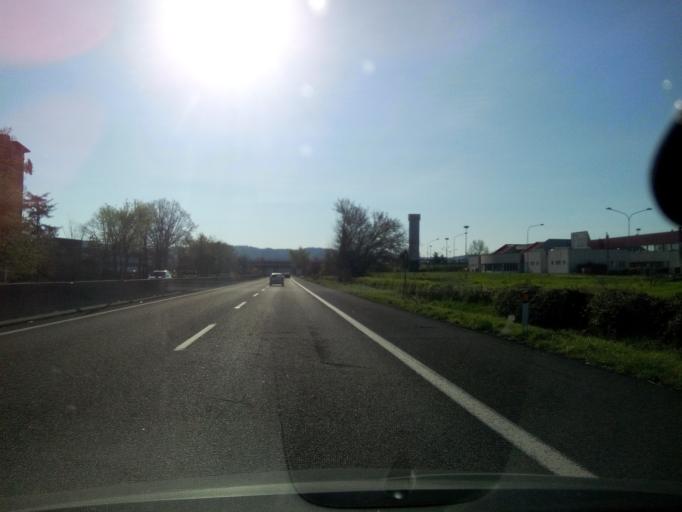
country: IT
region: Emilia-Romagna
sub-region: Provincia di Bologna
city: Riale
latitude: 44.4930
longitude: 11.2405
